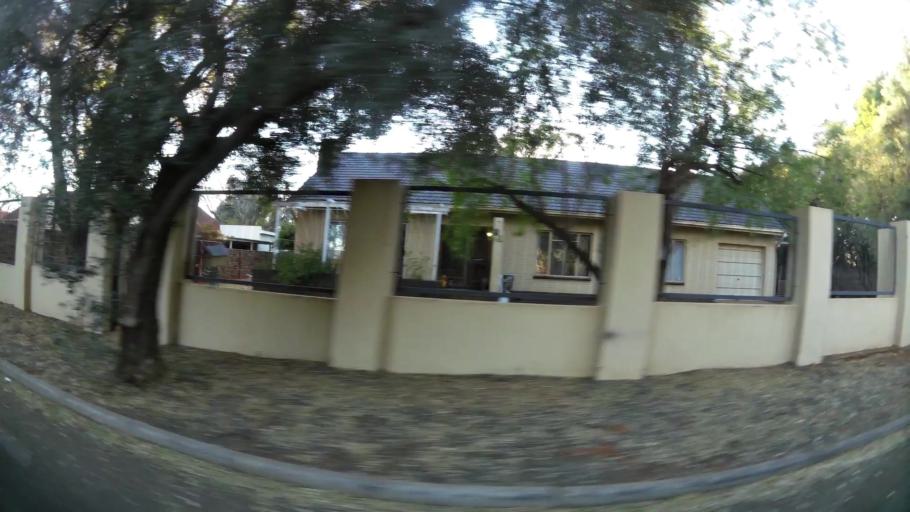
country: ZA
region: Northern Cape
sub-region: Frances Baard District Municipality
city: Kimberley
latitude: -28.7540
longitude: 24.7369
